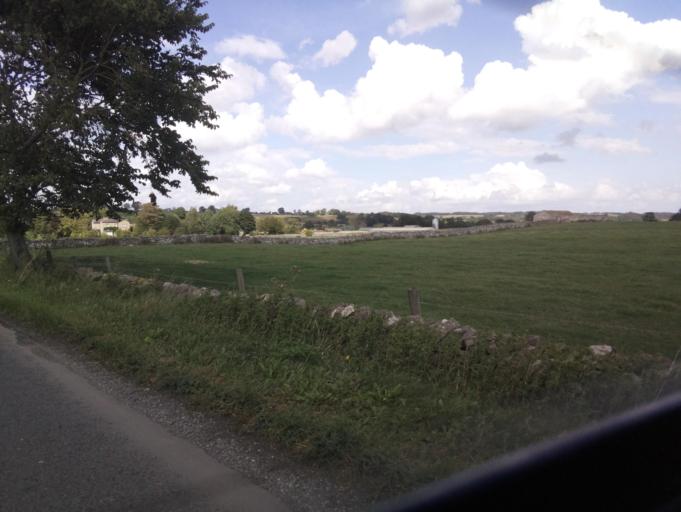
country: GB
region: England
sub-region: North Yorkshire
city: Leyburn
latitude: 54.3272
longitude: -1.8250
